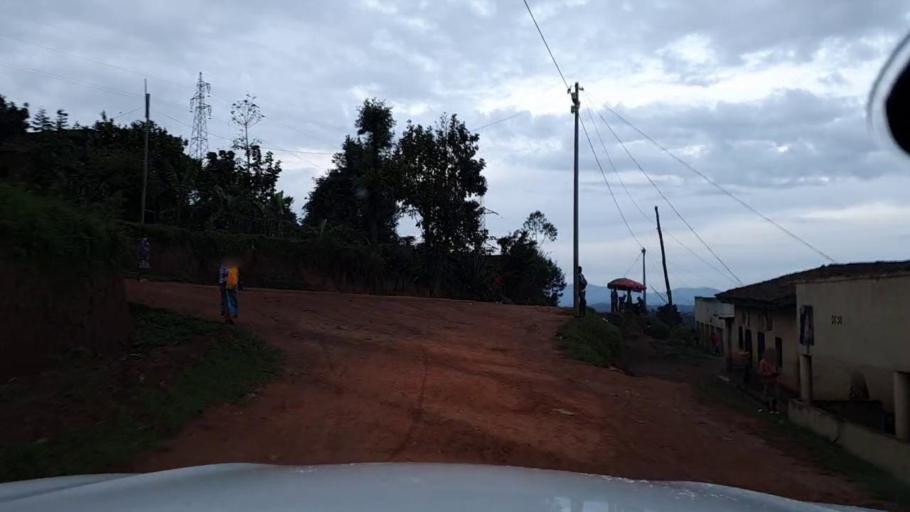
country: BI
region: Kayanza
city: Kayanza
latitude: -2.7126
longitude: 29.5408
